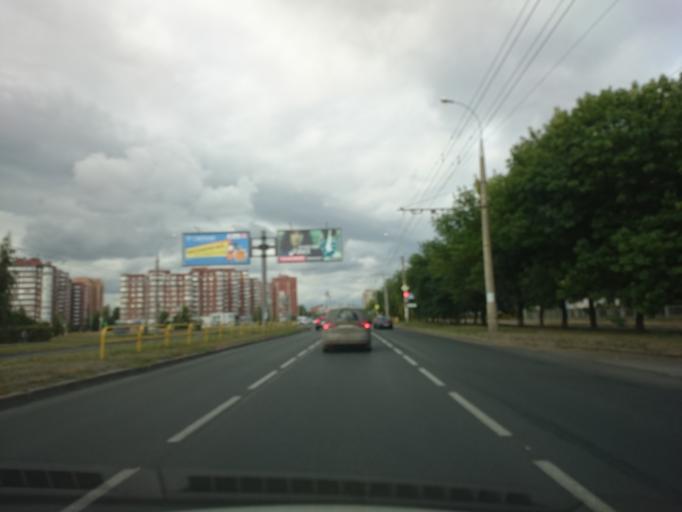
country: RU
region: Samara
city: Tol'yatti
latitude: 53.5115
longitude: 49.3053
